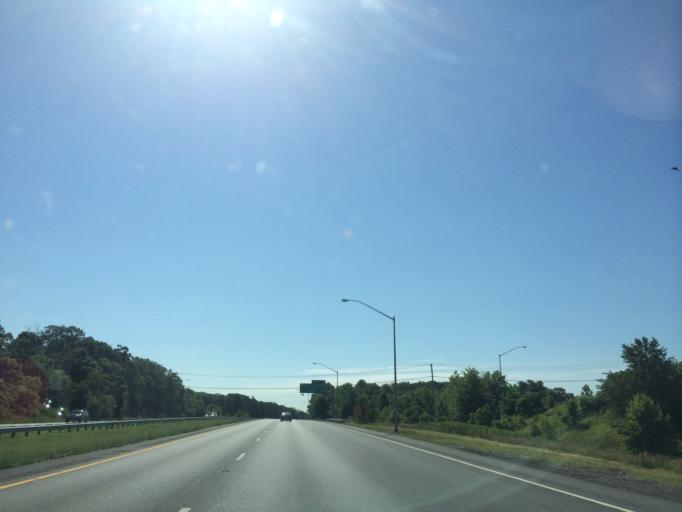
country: US
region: Maryland
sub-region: Anne Arundel County
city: Gambrills
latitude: 39.0802
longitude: -76.6774
